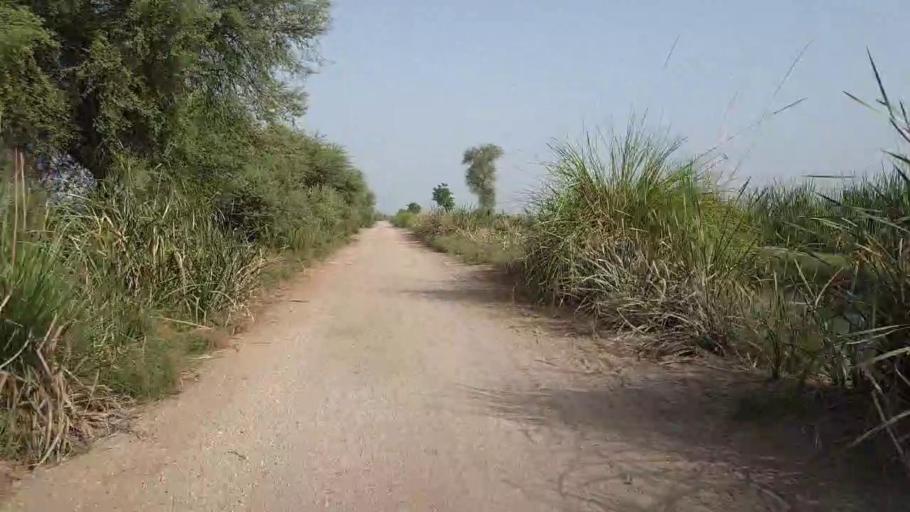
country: PK
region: Sindh
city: Daur
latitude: 26.3352
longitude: 68.1867
